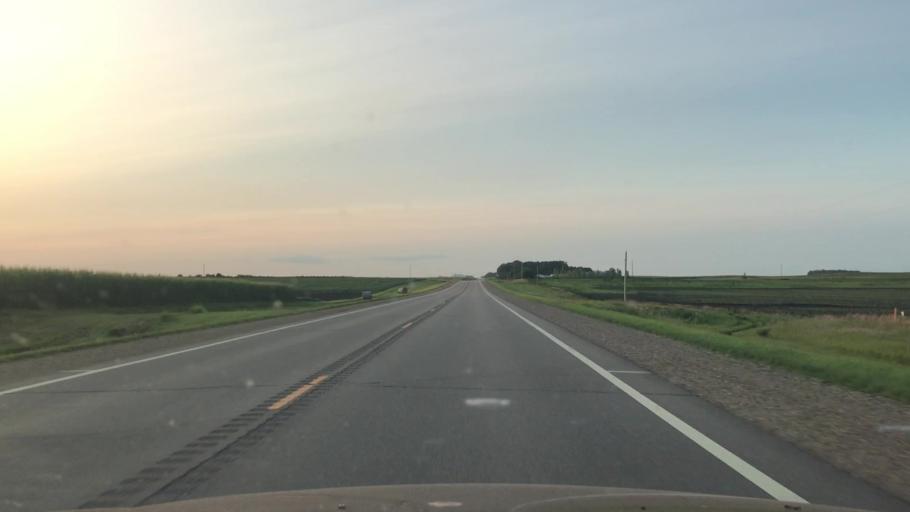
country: US
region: Minnesota
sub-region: Redwood County
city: Redwood Falls
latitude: 44.4376
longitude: -95.1176
